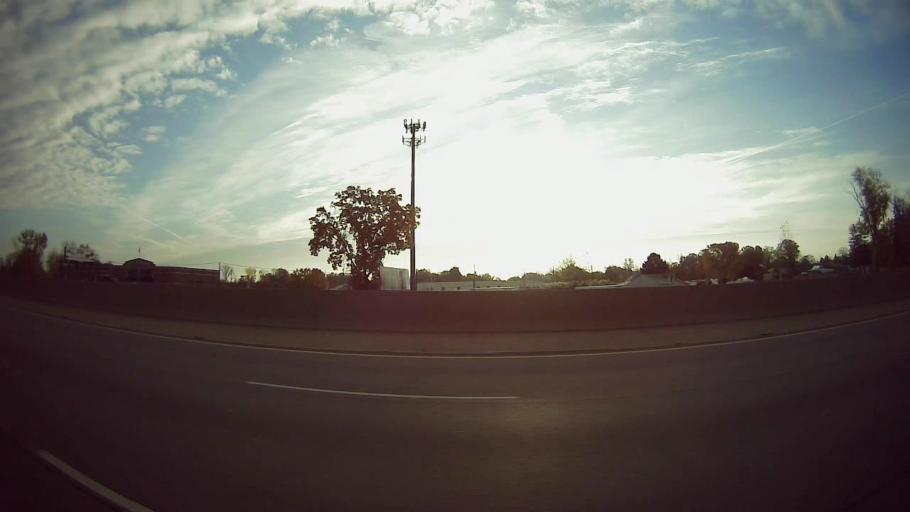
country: US
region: Michigan
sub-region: Macomb County
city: Saint Clair Shores
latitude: 42.5459
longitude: -82.8811
